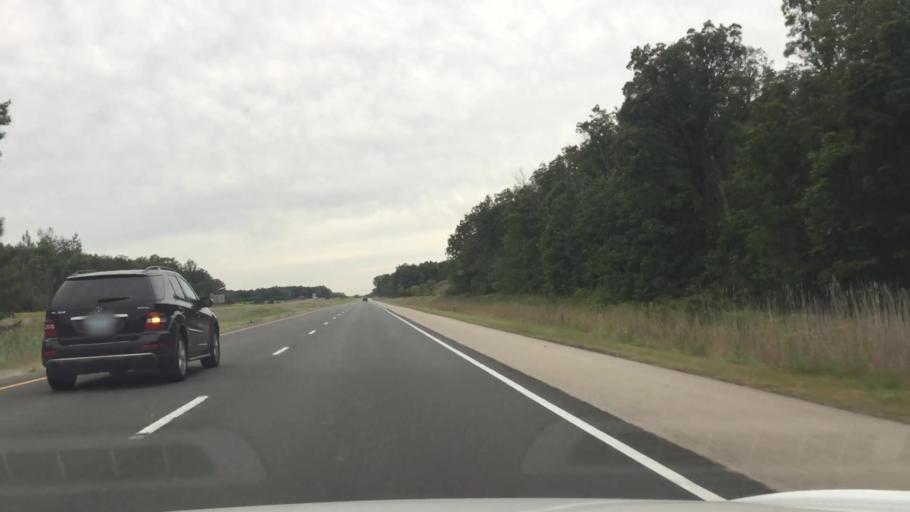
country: CA
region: Ontario
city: Lambton Shores
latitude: 42.9922
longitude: -81.8922
